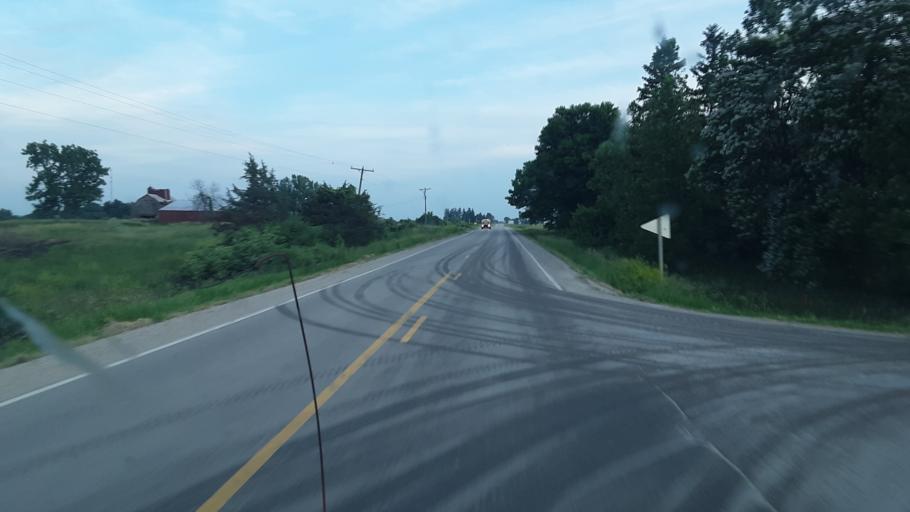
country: US
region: Iowa
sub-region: Iowa County
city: Marengo
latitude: 41.7176
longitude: -92.1828
